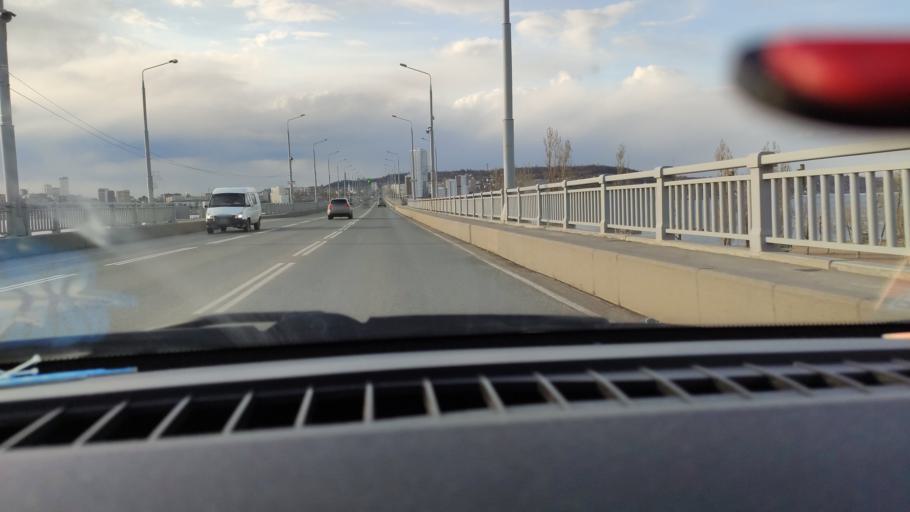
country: RU
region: Saratov
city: Engel's
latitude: 51.5176
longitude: 46.0695
